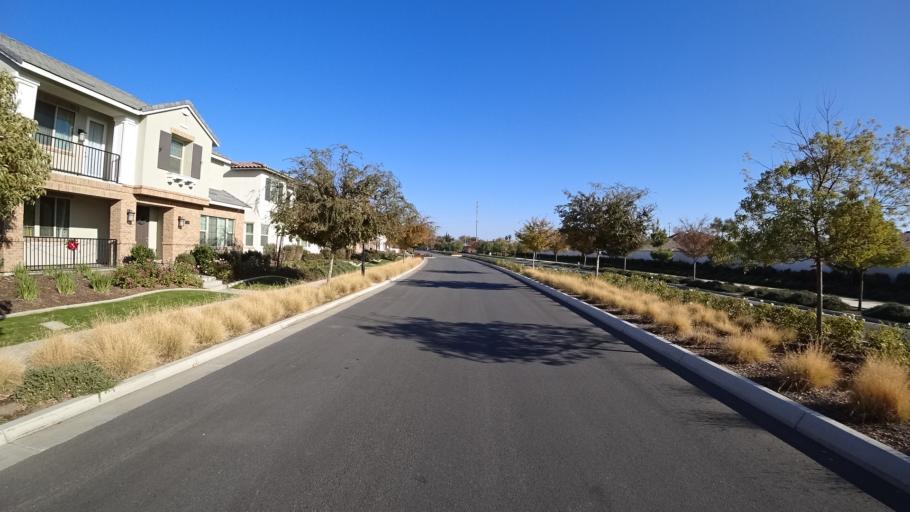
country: US
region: California
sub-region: Kern County
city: Rosedale
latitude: 35.3178
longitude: -119.1306
